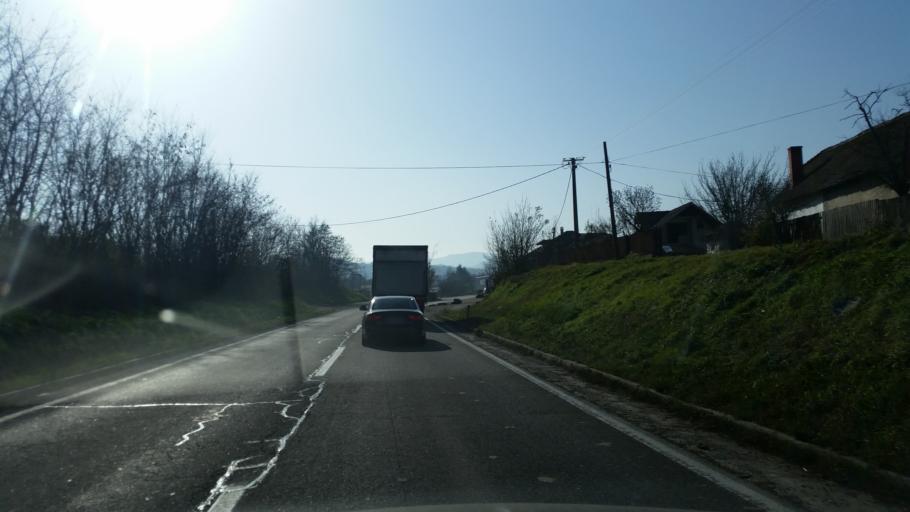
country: RS
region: Central Serbia
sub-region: Kolubarski Okrug
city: Ljig
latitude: 44.2556
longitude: 20.2863
